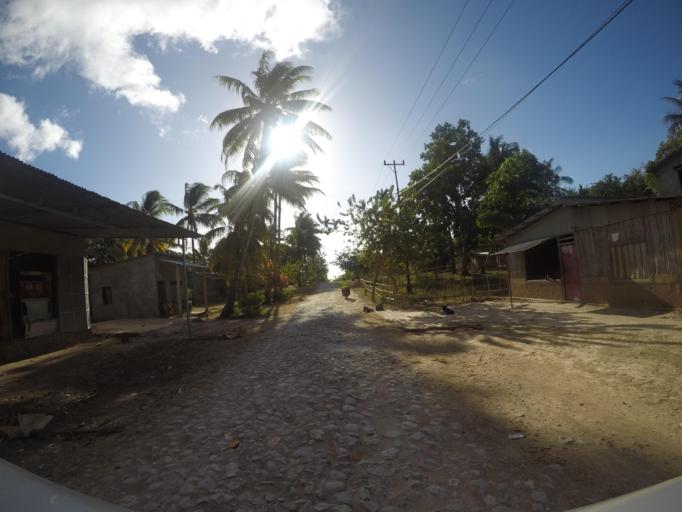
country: TL
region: Lautem
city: Lospalos
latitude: -8.4468
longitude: 126.8768
